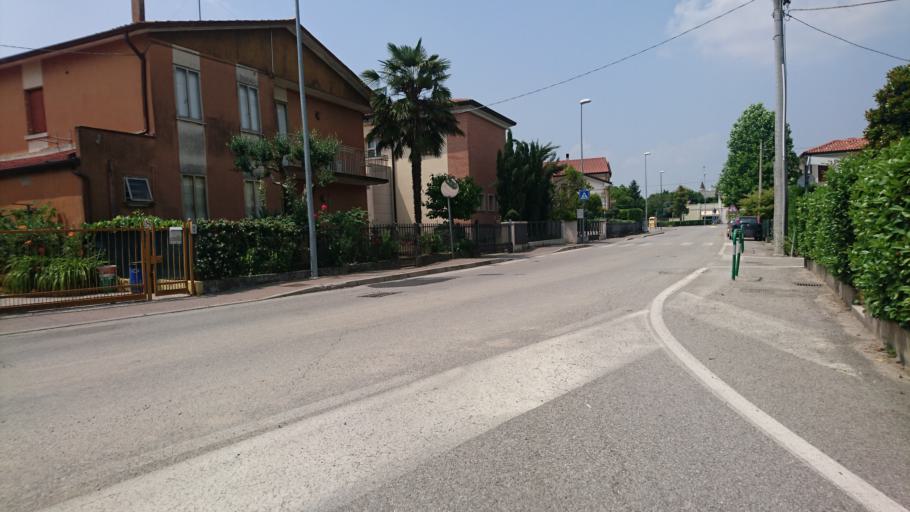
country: IT
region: Veneto
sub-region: Provincia di Padova
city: Cartura
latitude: 45.2665
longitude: 11.8648
